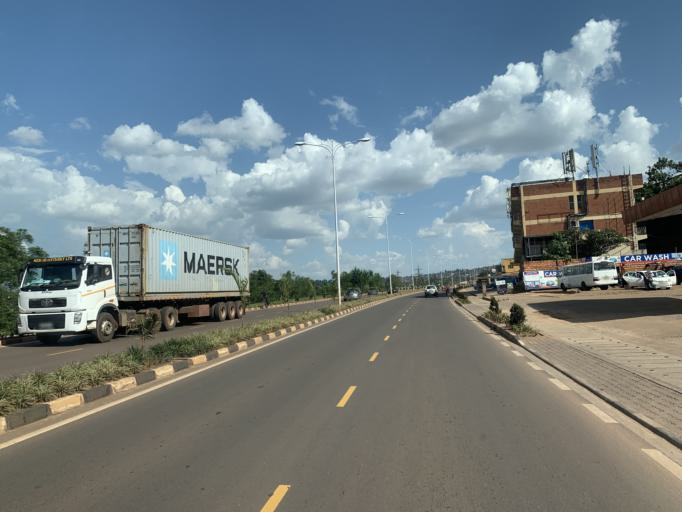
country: RW
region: Kigali
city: Kigali
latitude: -1.9655
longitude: 30.0808
